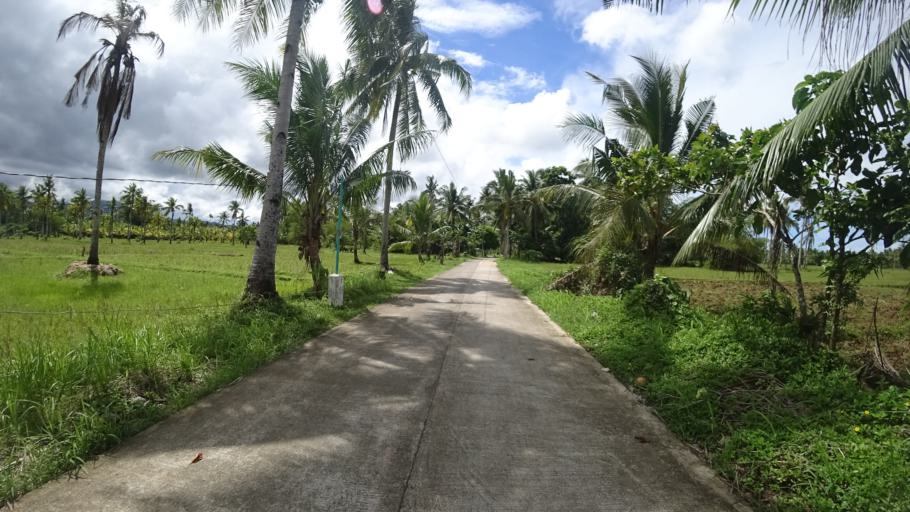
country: PH
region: Eastern Visayas
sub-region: Province of Leyte
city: MacArthur
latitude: 10.8481
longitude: 124.9640
